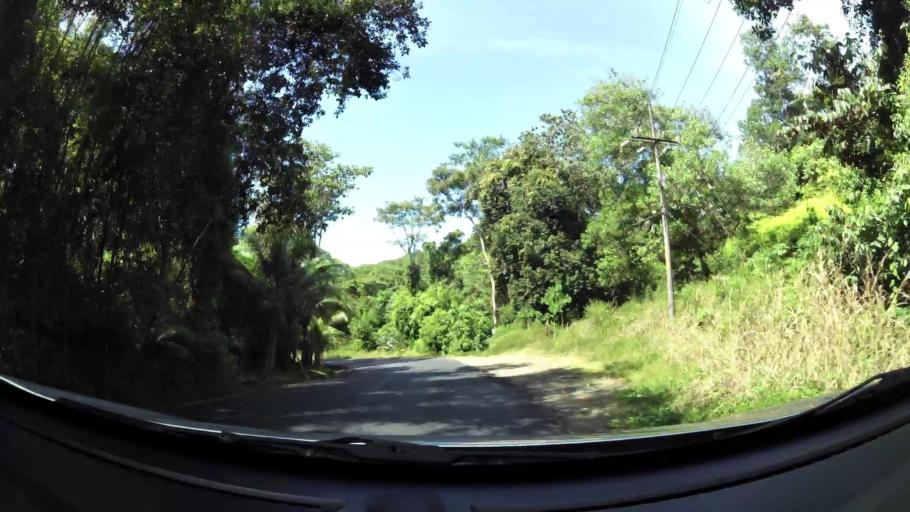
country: CR
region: San Jose
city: San Isidro
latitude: 9.2801
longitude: -83.8292
